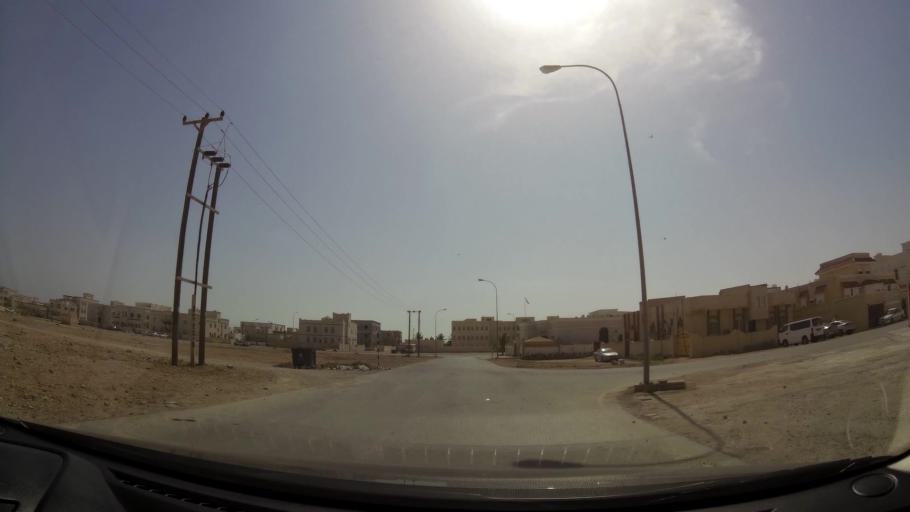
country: OM
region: Zufar
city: Salalah
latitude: 17.0447
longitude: 54.1524
